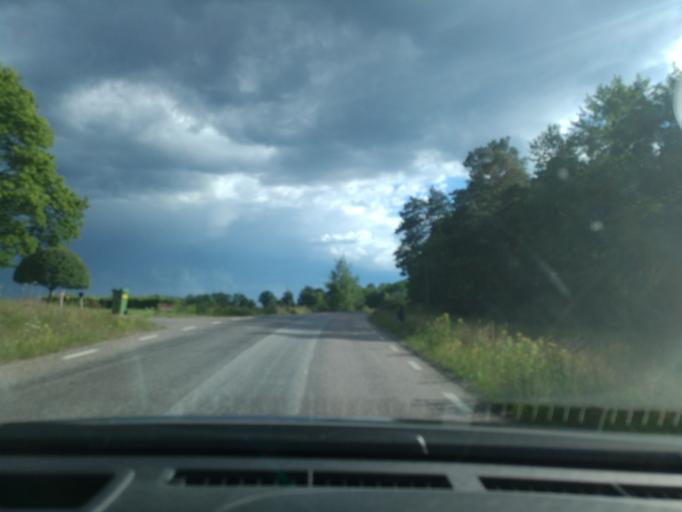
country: SE
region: Soedermanland
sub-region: Eskilstuna Kommun
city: Arla
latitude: 59.4137
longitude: 16.7001
